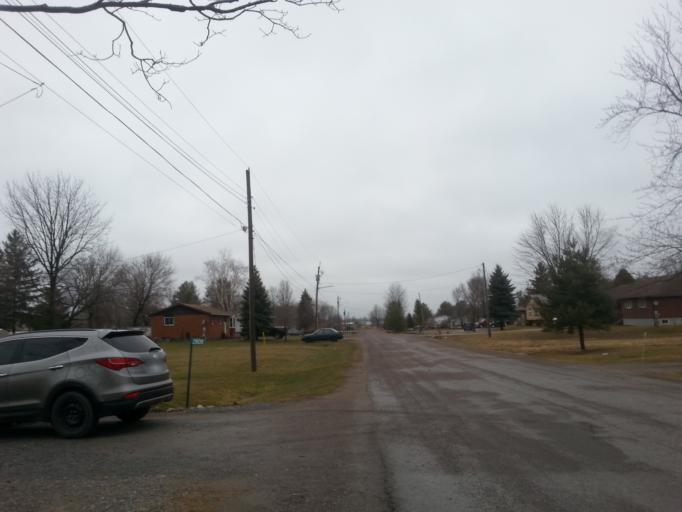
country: CA
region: Ontario
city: Orillia
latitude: 44.5493
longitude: -79.1760
